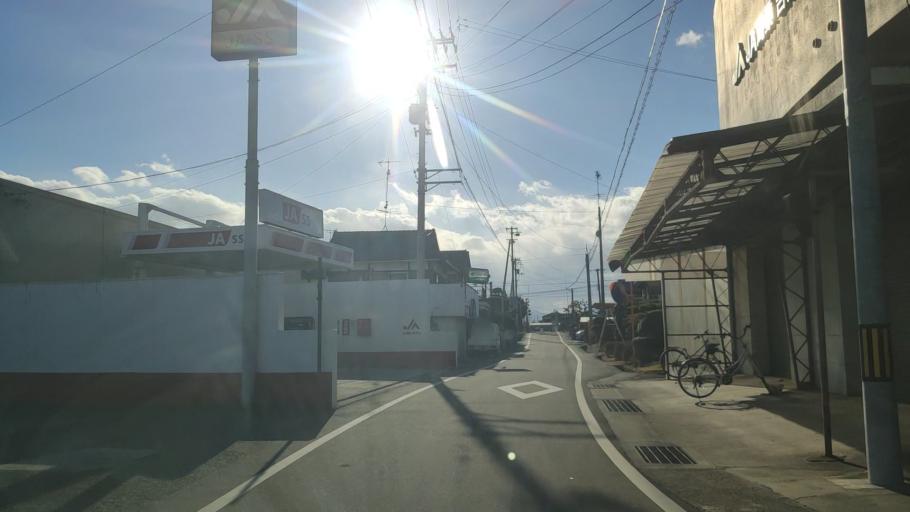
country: JP
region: Ehime
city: Saijo
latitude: 33.9130
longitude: 133.0999
